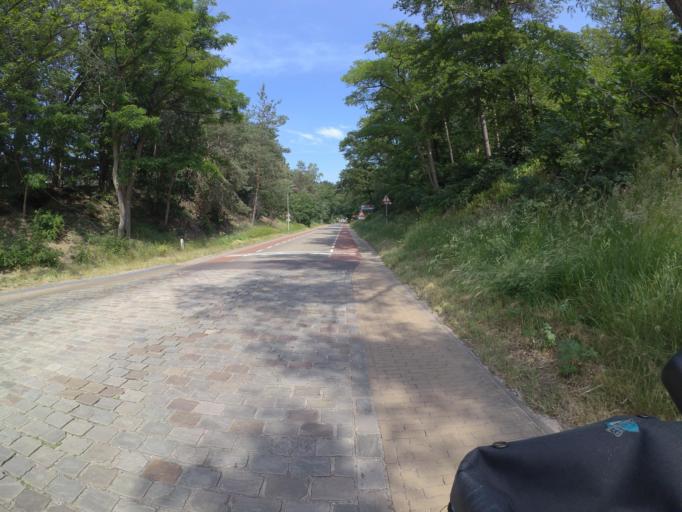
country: NL
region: Overijssel
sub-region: Gemeente Twenterand
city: Den Ham
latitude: 52.3875
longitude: 6.4360
